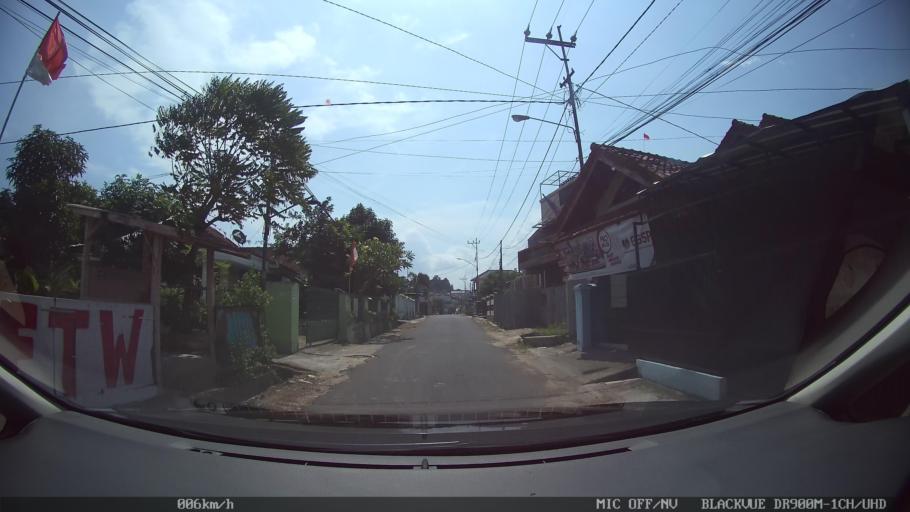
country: ID
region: Lampung
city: Kedaton
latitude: -5.3984
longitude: 105.2595
